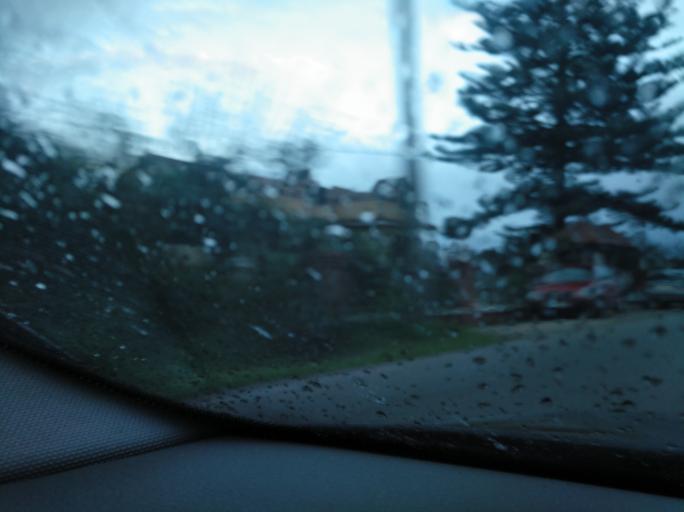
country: PT
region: Faro
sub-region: Vila Real de Santo Antonio
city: Monte Gordo
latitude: 37.1910
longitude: -7.4842
